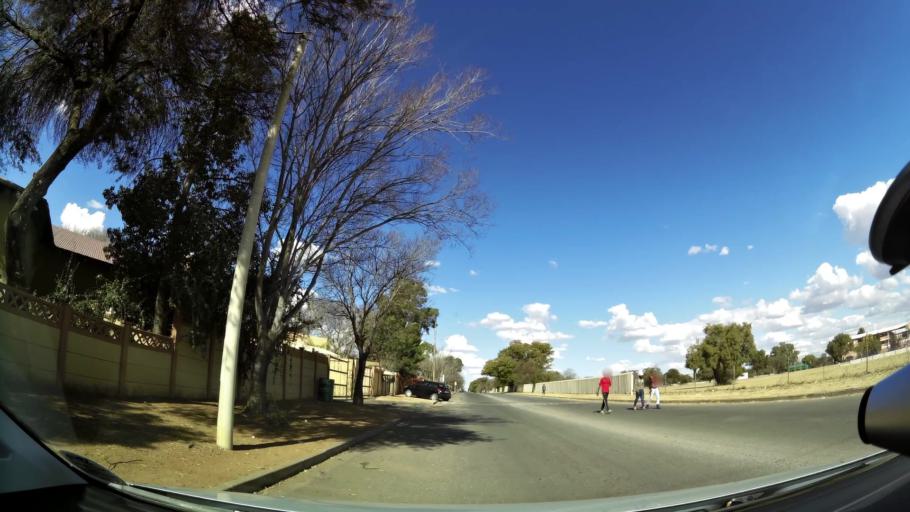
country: ZA
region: North-West
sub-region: Dr Kenneth Kaunda District Municipality
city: Klerksdorp
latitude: -26.8587
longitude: 26.6453
